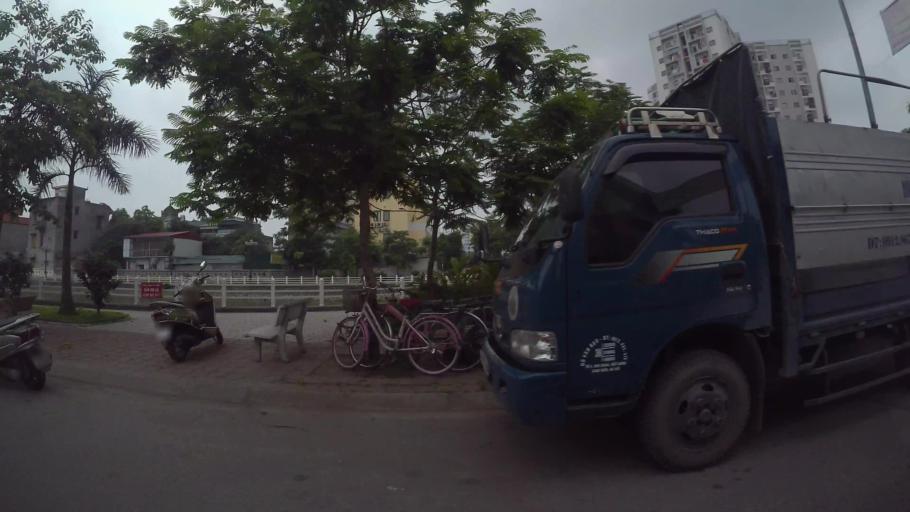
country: VN
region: Ha Noi
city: Trau Quy
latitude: 21.0603
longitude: 105.9151
